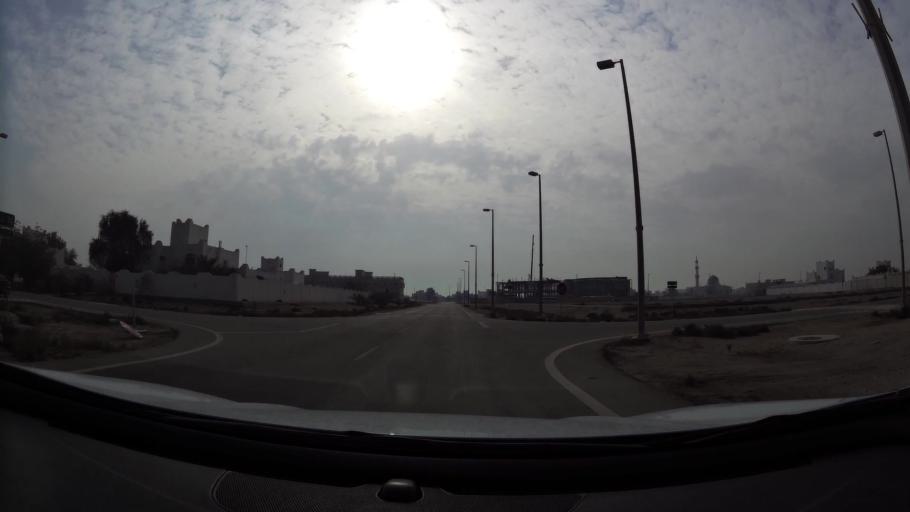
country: AE
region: Abu Dhabi
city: Abu Dhabi
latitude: 24.6726
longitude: 54.7708
